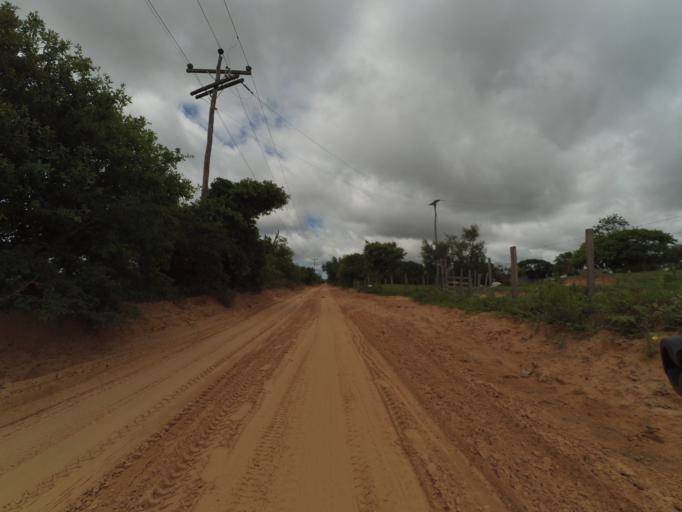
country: BO
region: Santa Cruz
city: Santa Rita
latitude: -17.9060
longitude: -63.2444
